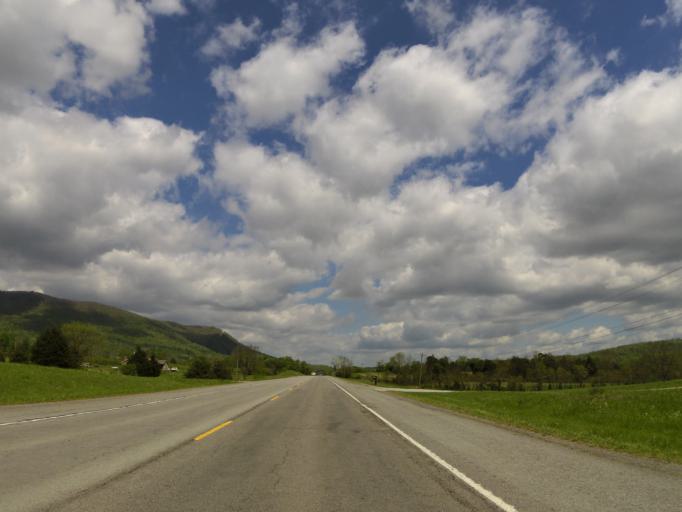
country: US
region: Tennessee
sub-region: Campbell County
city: Fincastle
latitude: 36.4525
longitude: -83.9167
